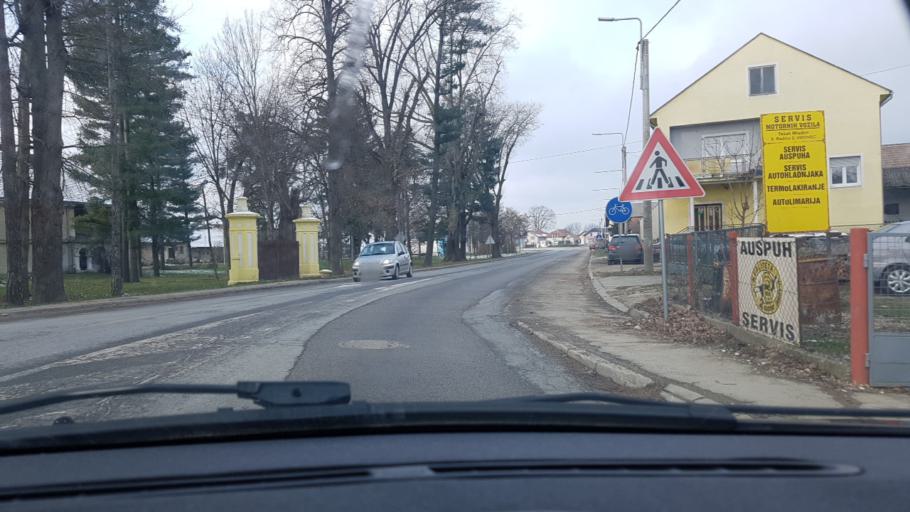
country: HR
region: Varazdinska
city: Nedeljanec
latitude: 46.2857
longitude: 16.2550
